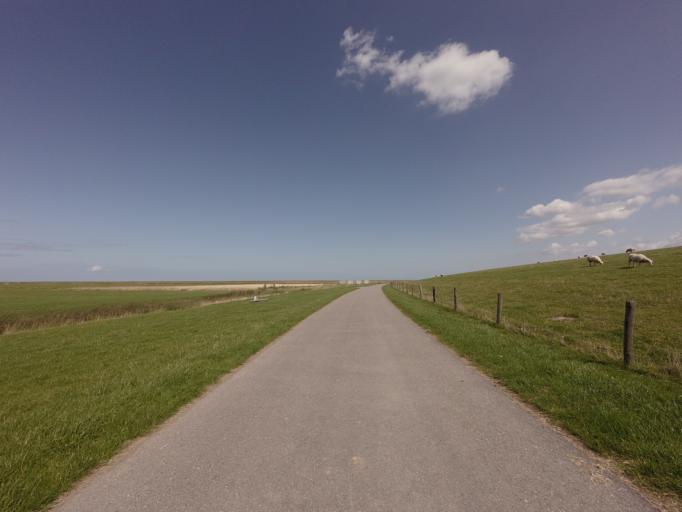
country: NL
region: Friesland
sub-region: Gemeente Ferwerderadiel
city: Marrum
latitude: 53.3372
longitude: 5.7829
